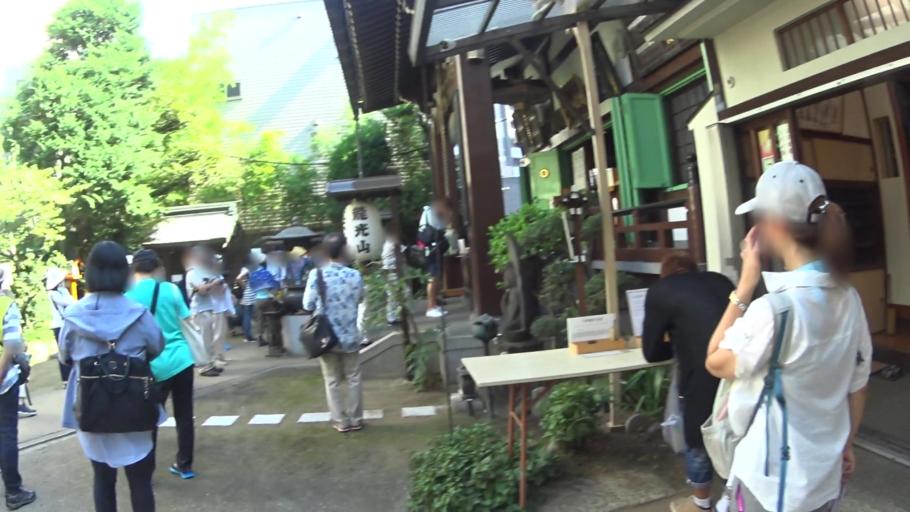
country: JP
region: Saitama
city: Soka
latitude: 35.7242
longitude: 139.7916
